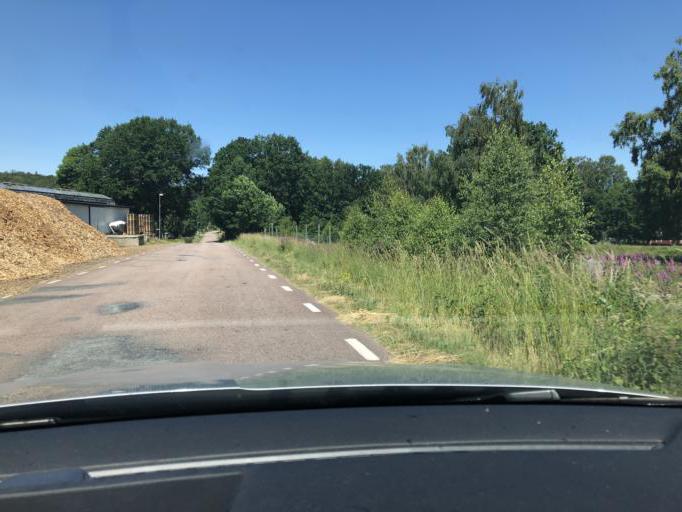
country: SE
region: Blekinge
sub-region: Solvesborgs Kommun
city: Soelvesborg
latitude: 56.1583
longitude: 14.6009
